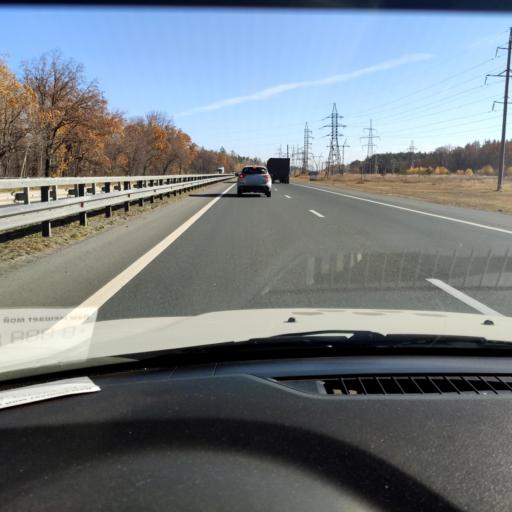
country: RU
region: Samara
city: Pribrezhnyy
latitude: 53.5185
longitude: 49.8114
